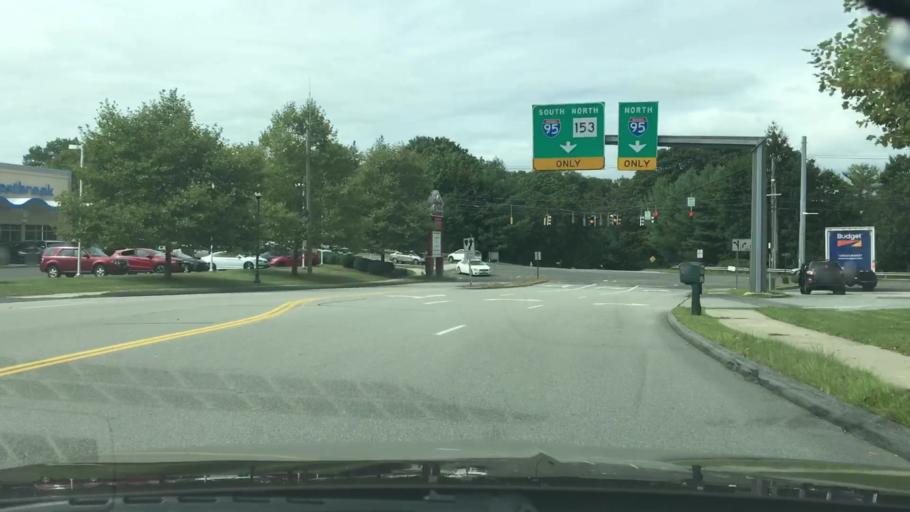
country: US
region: Connecticut
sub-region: Middlesex County
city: Westbrook Center
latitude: 41.2900
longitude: -72.4447
